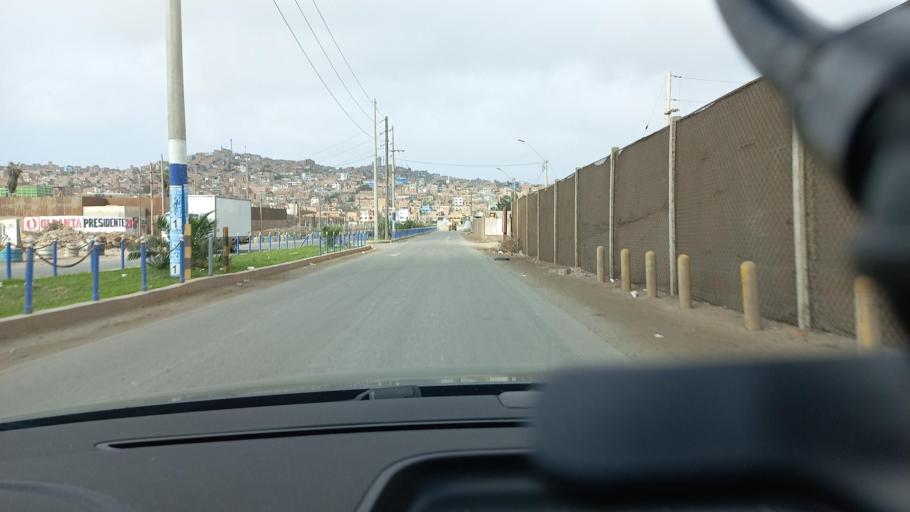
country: PE
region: Lima
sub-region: Lima
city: Surco
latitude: -12.2024
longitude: -76.9981
